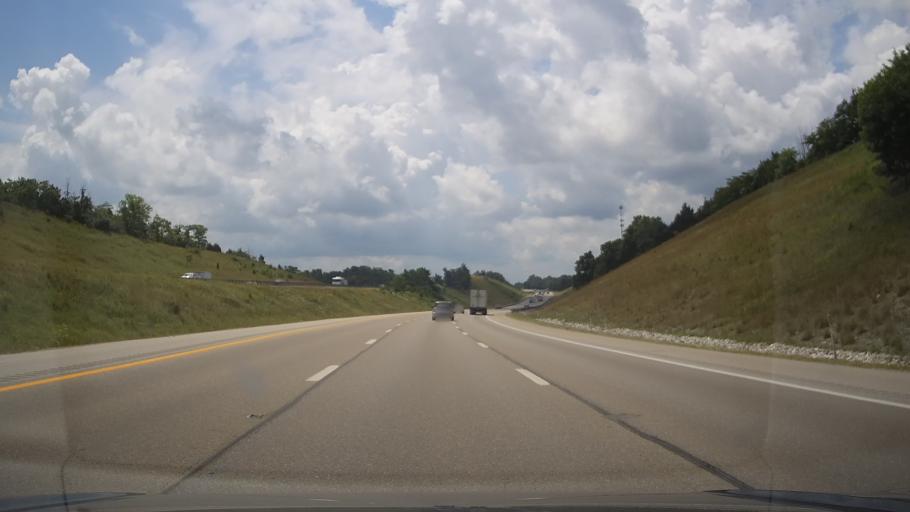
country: US
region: Kentucky
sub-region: Grant County
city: Williamstown
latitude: 38.5677
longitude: -84.5938
